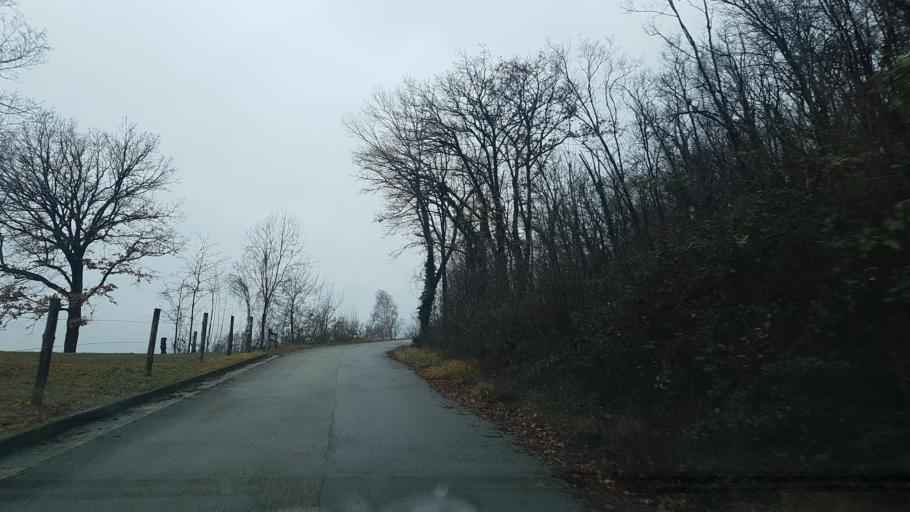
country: IT
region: Friuli Venezia Giulia
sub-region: Provincia di Udine
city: San Pietro al Natisone
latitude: 46.0852
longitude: 13.4837
